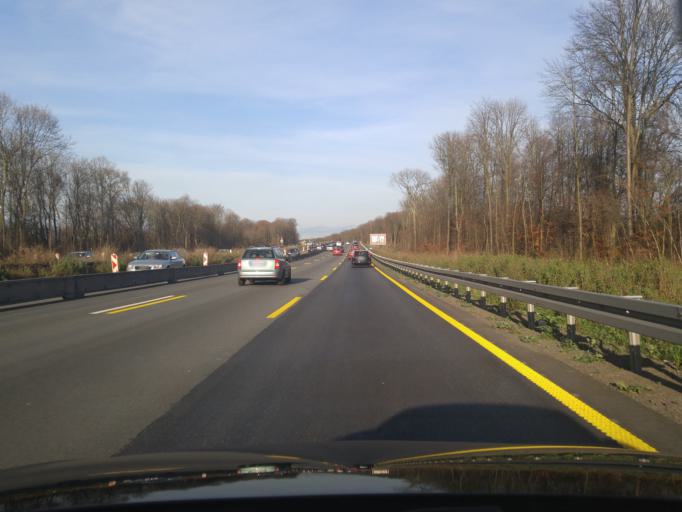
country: DE
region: North Rhine-Westphalia
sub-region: Regierungsbezirk Koln
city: Muelheim
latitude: 50.9994
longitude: 7.0134
